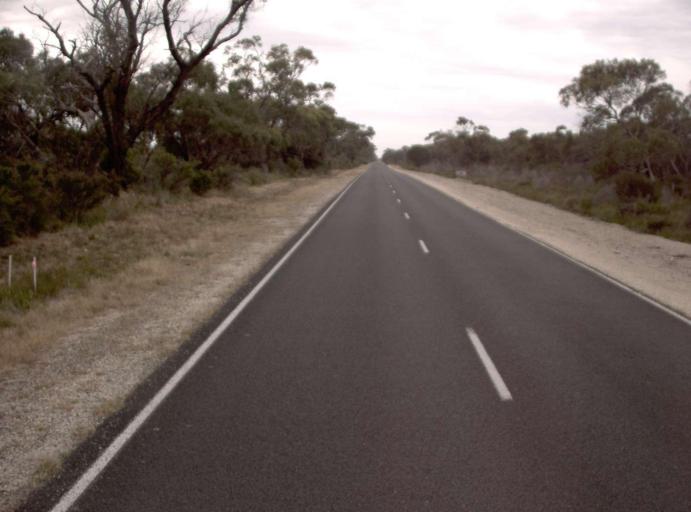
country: AU
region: Victoria
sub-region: Wellington
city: Sale
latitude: -38.1388
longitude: 147.4095
